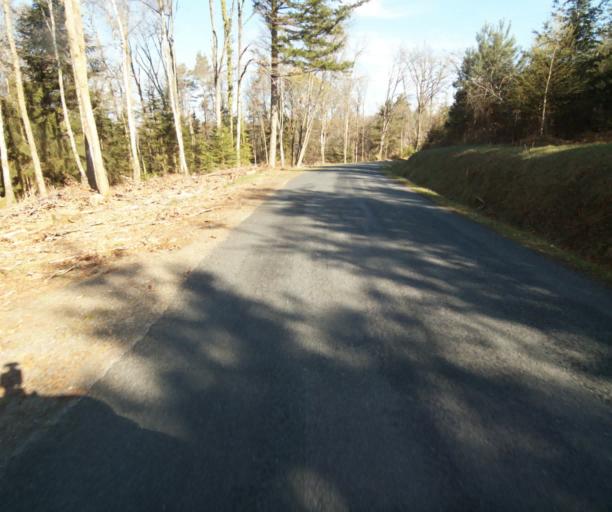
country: FR
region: Limousin
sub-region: Departement de la Correze
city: Correze
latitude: 45.2908
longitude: 1.8693
